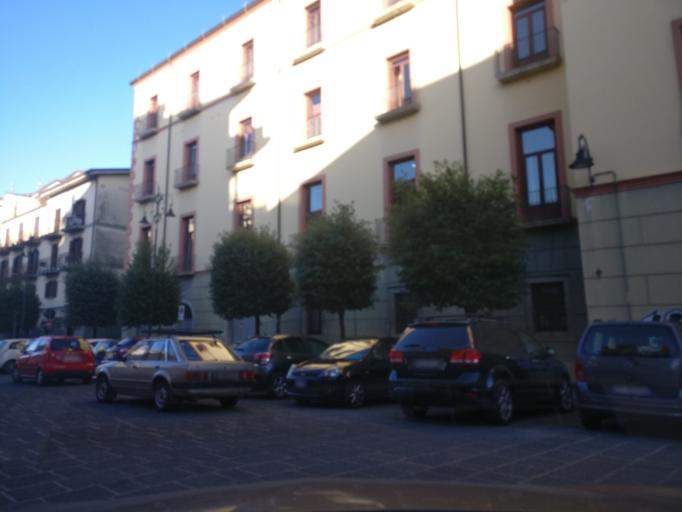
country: IT
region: Campania
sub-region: Provincia di Avellino
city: Avellino
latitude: 40.9150
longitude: 14.7919
